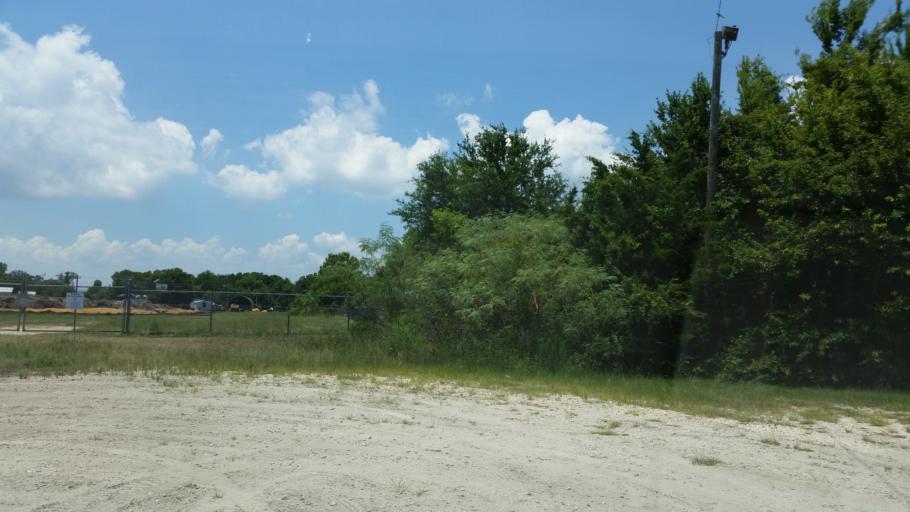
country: US
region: Florida
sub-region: Escambia County
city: Pensacola
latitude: 30.4047
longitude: -87.2361
